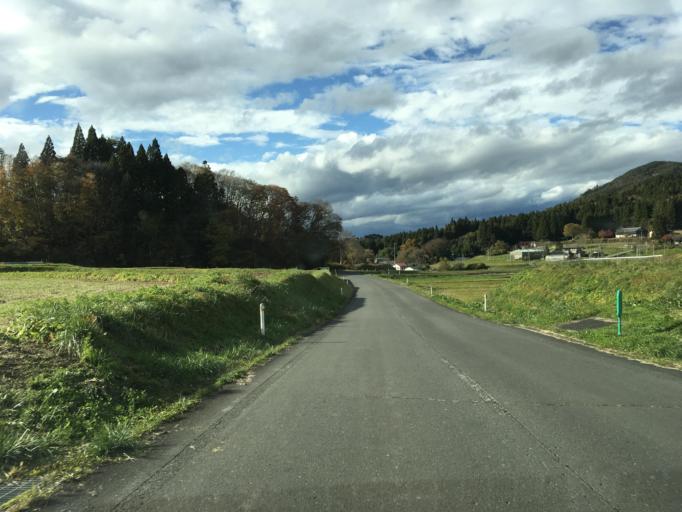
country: JP
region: Iwate
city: Ofunato
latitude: 38.8906
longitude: 141.4540
